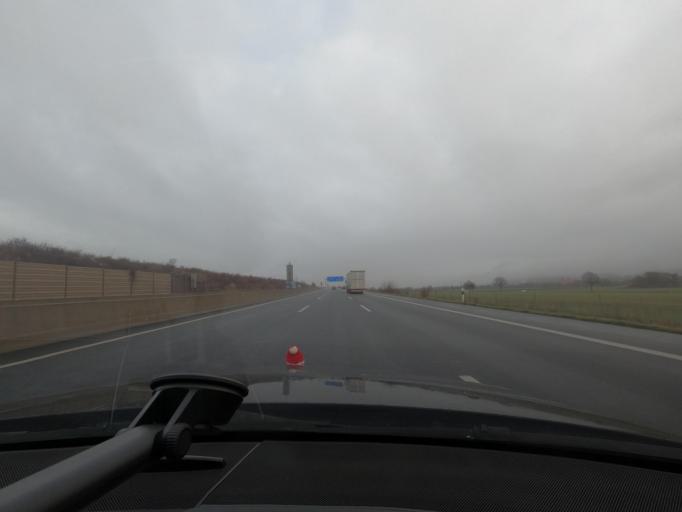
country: DE
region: Lower Saxony
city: Norten-Hardenberg
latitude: 51.6187
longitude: 9.9112
